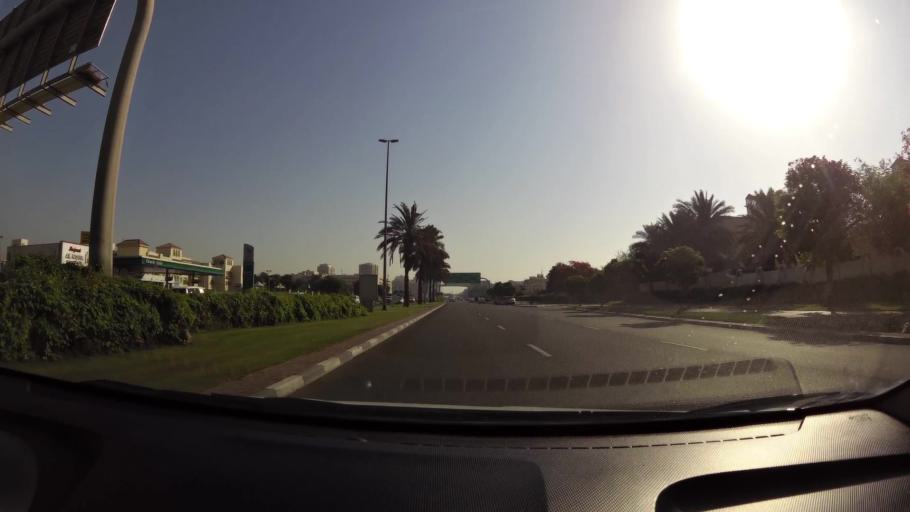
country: AE
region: Ash Shariqah
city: Sharjah
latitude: 25.2640
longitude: 55.3752
